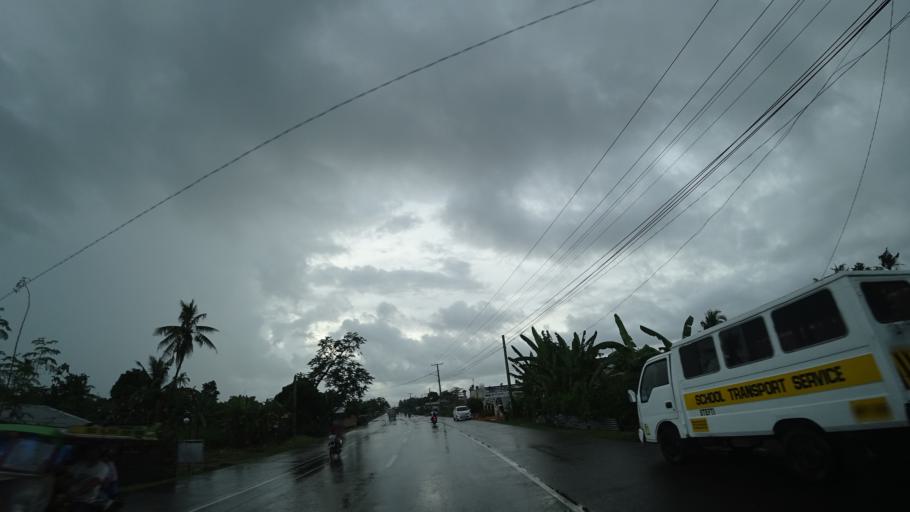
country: PH
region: Eastern Visayas
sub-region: Province of Leyte
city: Tanauan
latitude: 11.1228
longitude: 125.0150
